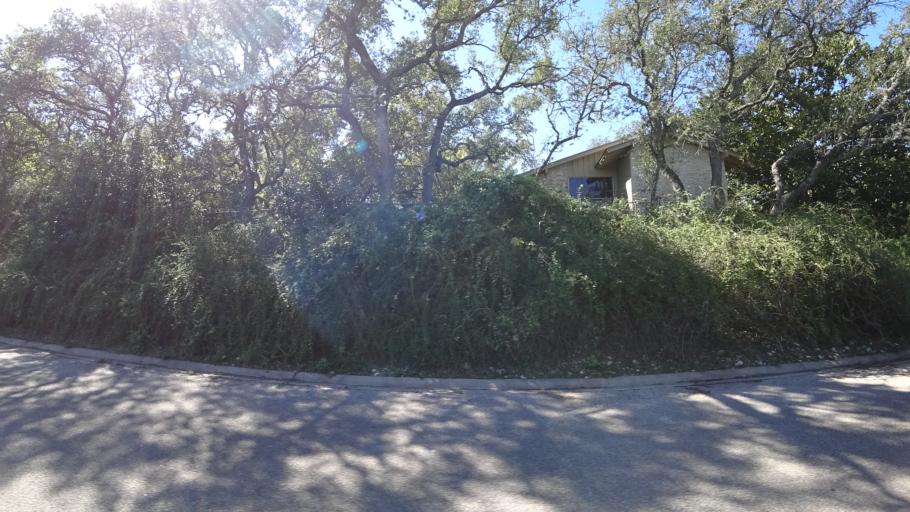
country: US
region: Texas
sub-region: Travis County
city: West Lake Hills
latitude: 30.3186
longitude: -97.7984
